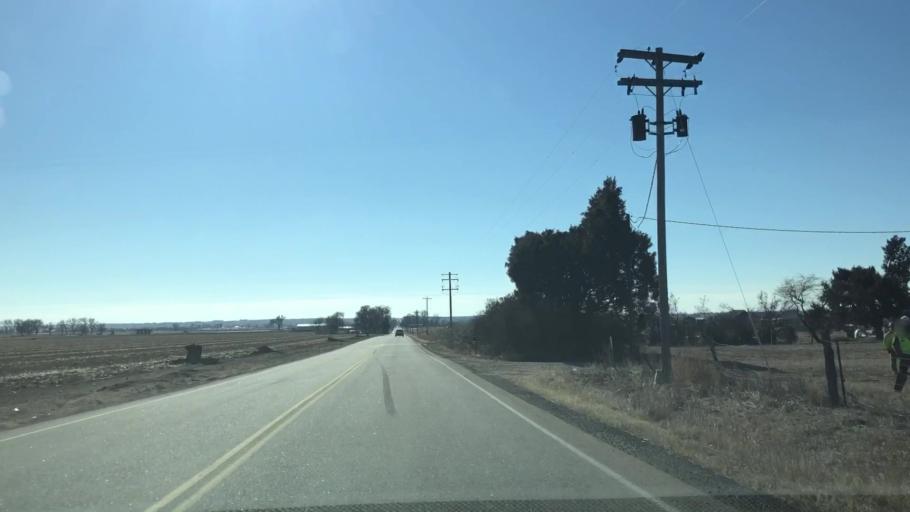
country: US
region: Colorado
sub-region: Weld County
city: Windsor
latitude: 40.5182
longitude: -104.9443
